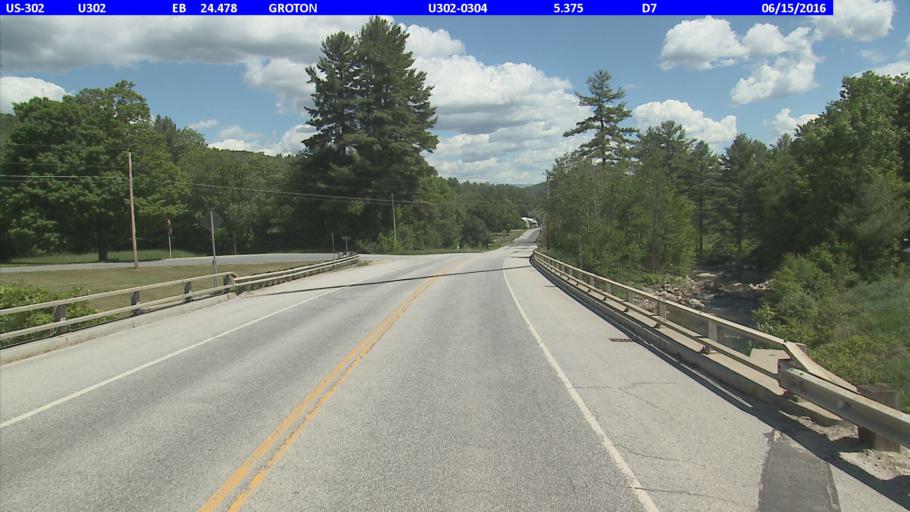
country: US
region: New Hampshire
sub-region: Grafton County
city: Woodsville
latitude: 44.2187
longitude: -72.2146
